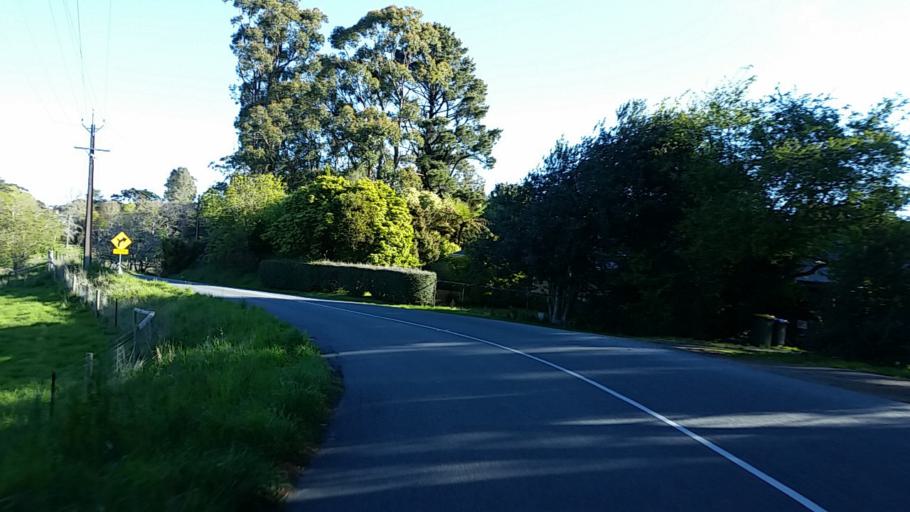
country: AU
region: South Australia
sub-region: Adelaide Hills
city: Adelaide Hills
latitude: -34.9356
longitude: 138.7421
